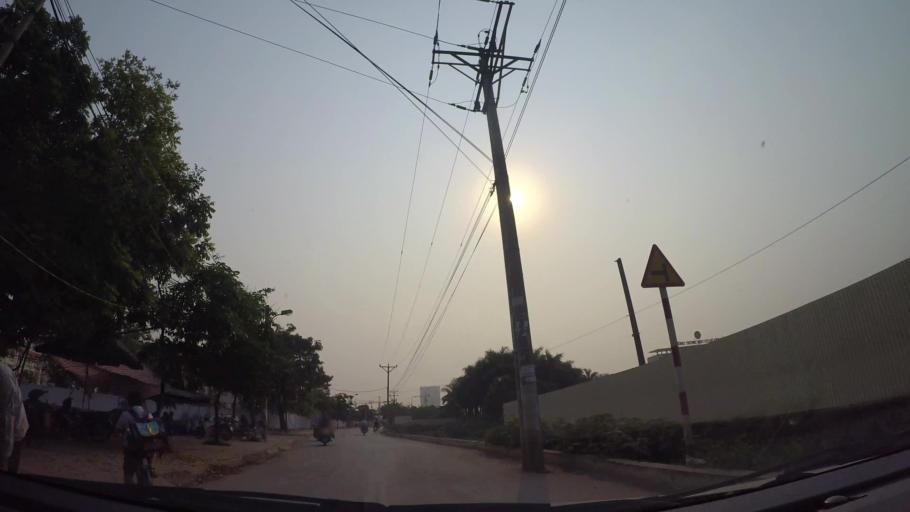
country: VN
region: Ha Noi
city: Cau Dien
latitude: 21.0058
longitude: 105.7457
